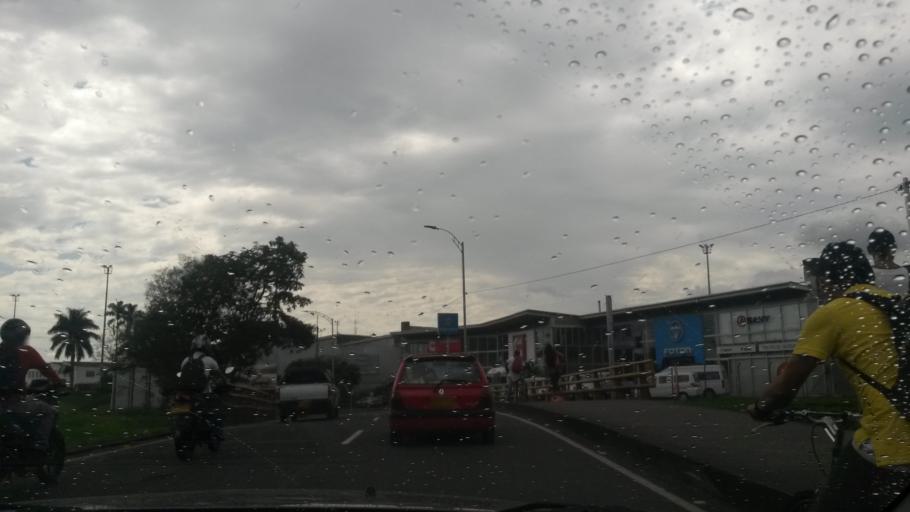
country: CO
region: Risaralda
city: Pereira
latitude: 4.8220
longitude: -75.6843
